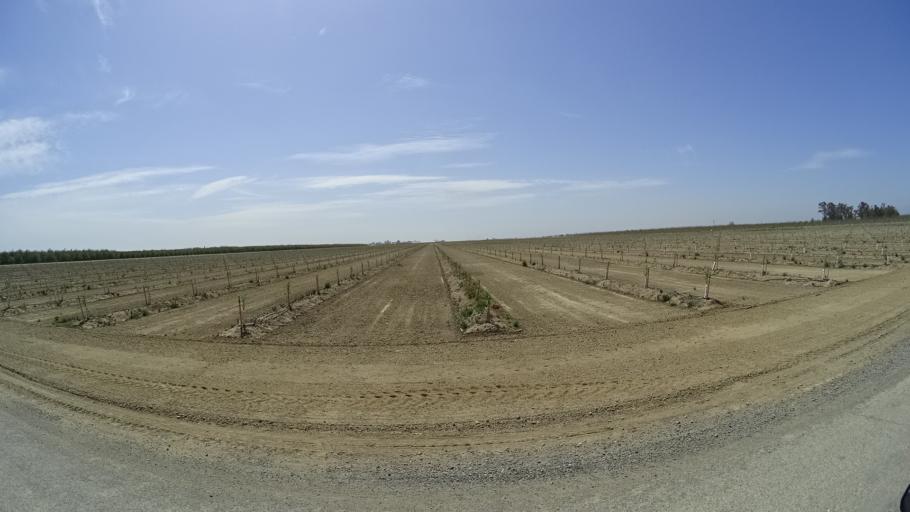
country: US
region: California
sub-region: Glenn County
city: Hamilton City
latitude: 39.6380
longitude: -122.0668
